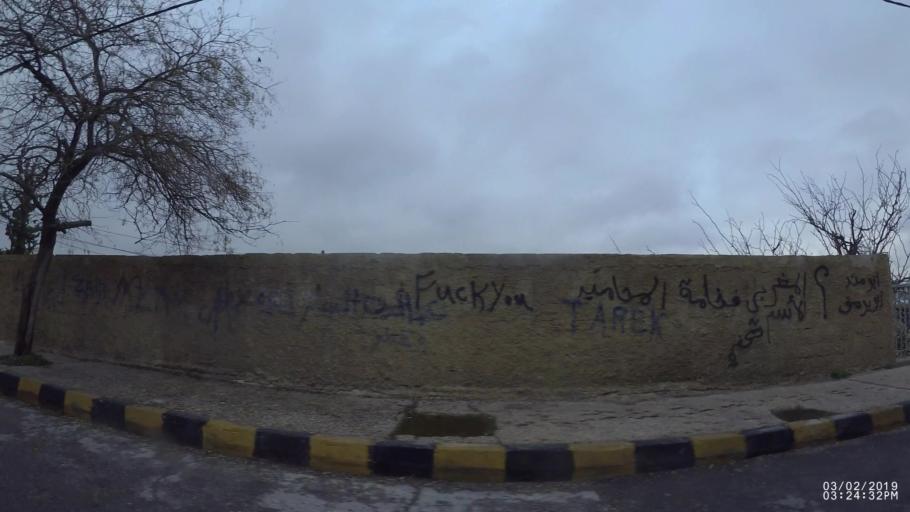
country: JO
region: Amman
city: Amman
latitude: 31.9566
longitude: 35.9342
